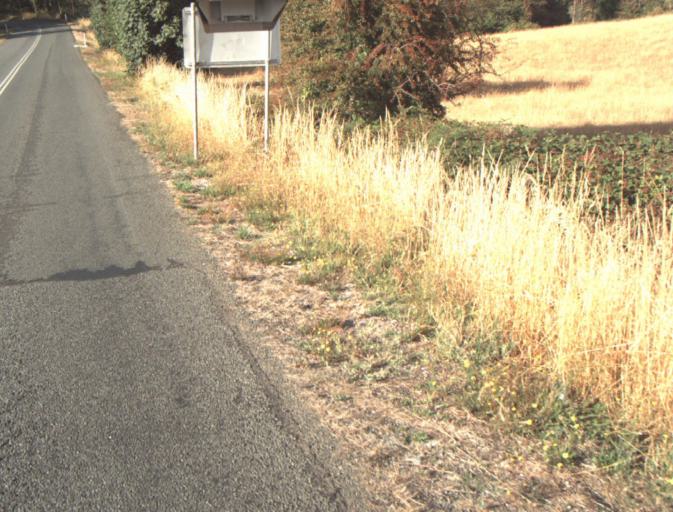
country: AU
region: Tasmania
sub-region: Dorset
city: Bridport
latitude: -41.1705
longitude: 147.2302
